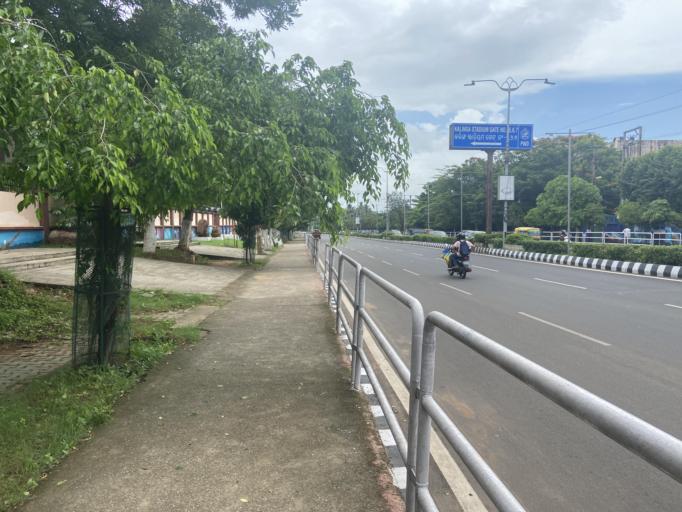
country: IN
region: Odisha
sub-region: Khordha
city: Bhubaneshwar
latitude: 20.2909
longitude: 85.8259
